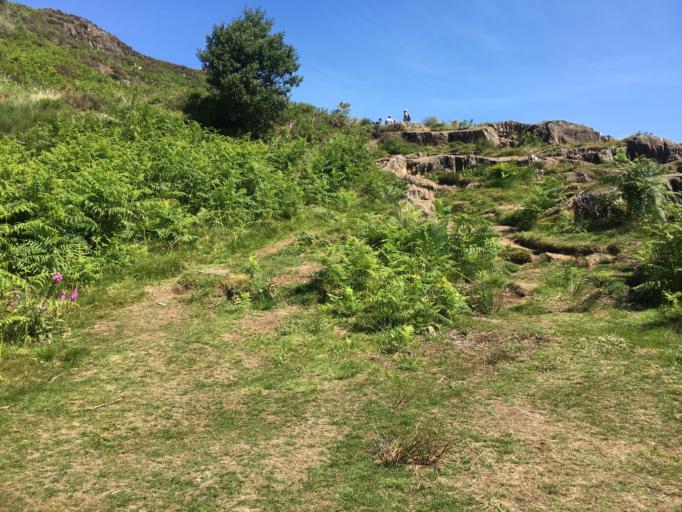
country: GB
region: Wales
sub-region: Gwynedd
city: Penrhyndeudraeth
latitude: 53.0009
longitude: -4.0869
